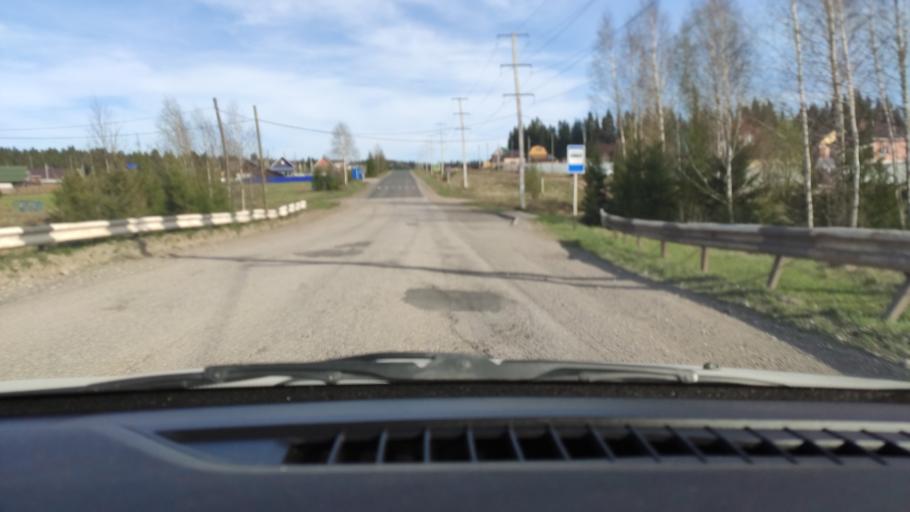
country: RU
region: Perm
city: Novyye Lyady
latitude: 57.9370
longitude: 56.6279
